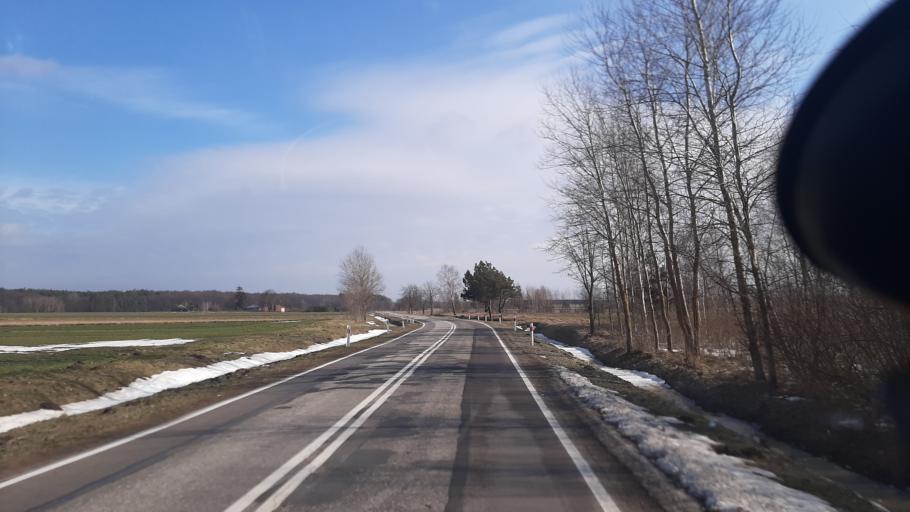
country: PL
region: Lublin Voivodeship
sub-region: Powiat wlodawski
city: Hansk
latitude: 51.4767
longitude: 23.3041
